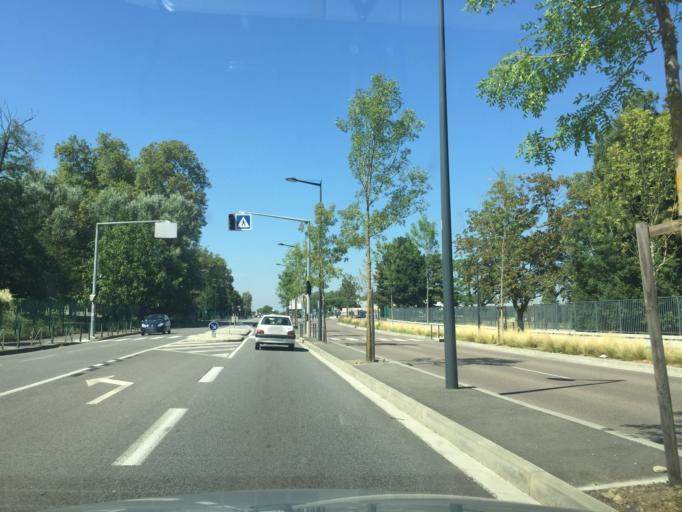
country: FR
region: Midi-Pyrenees
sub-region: Departement de la Haute-Garonne
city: Ramonville-Saint-Agne
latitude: 43.5586
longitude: 1.4641
